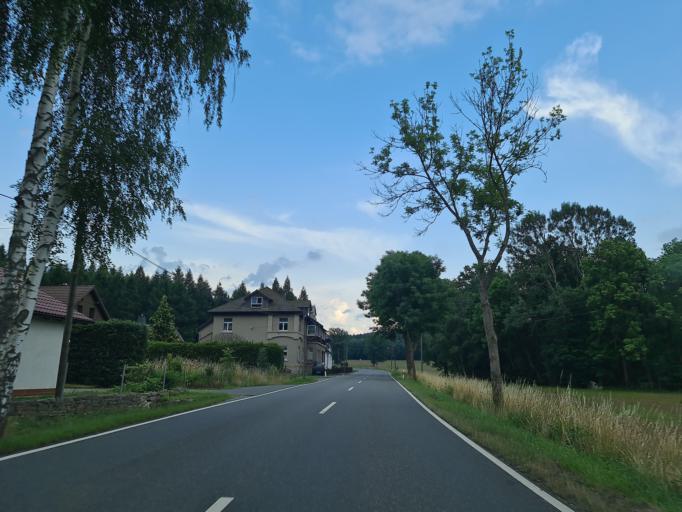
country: DE
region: Saxony
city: Bergen
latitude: 50.4638
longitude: 12.2866
